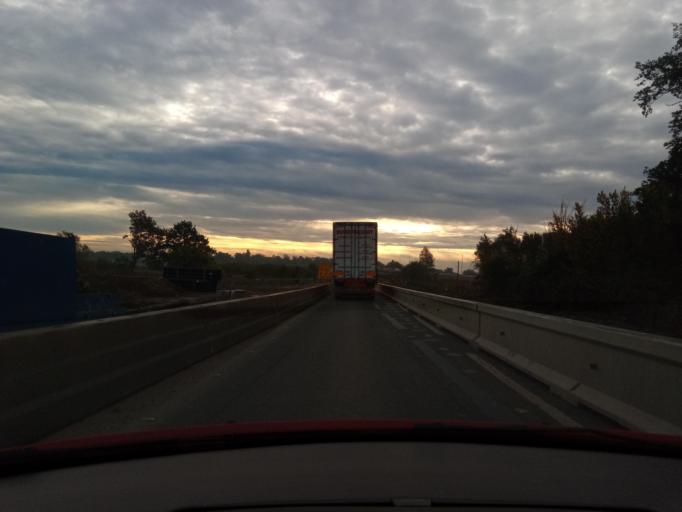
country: GB
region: England
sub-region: Cambridgeshire
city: Girton
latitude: 52.2342
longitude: 0.0705
